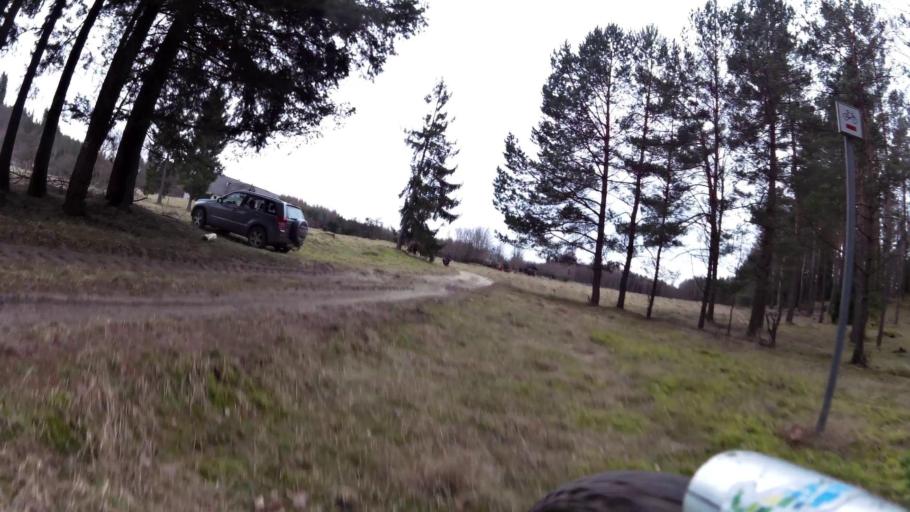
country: PL
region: Pomeranian Voivodeship
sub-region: Powiat bytowski
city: Trzebielino
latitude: 54.1214
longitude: 17.1292
